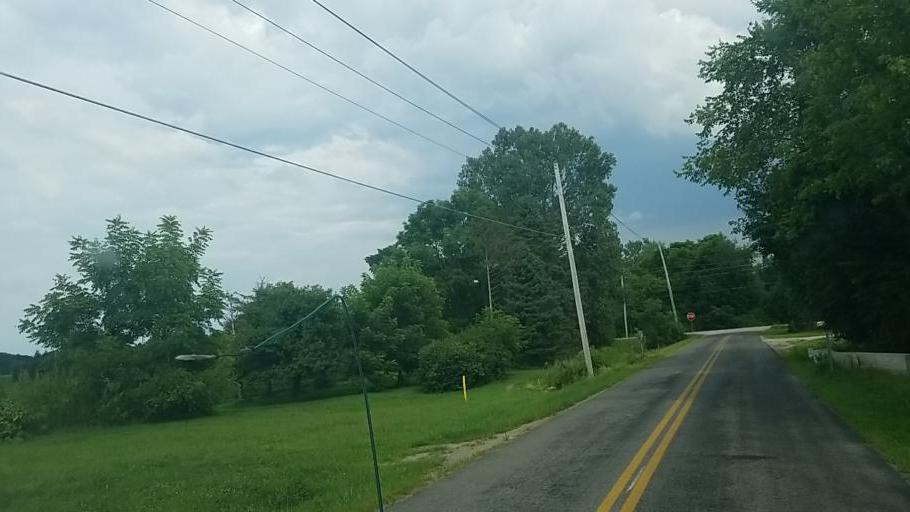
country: US
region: Ohio
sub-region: Wayne County
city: Creston
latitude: 40.9953
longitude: -81.8908
